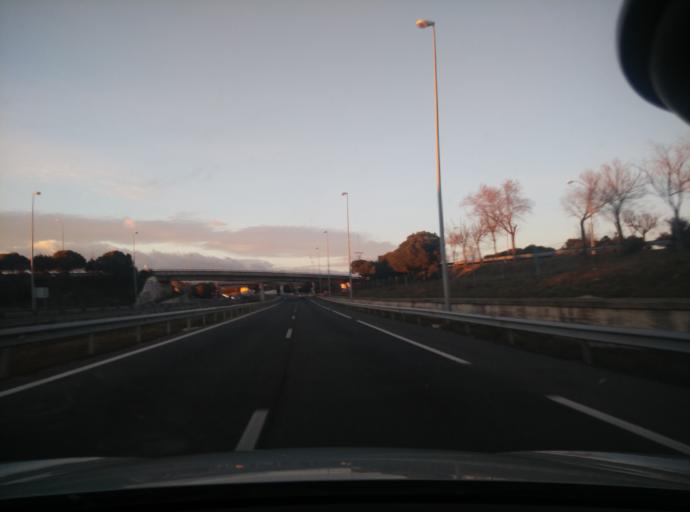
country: ES
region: Madrid
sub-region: Provincia de Madrid
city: Tres Cantos
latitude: 40.6060
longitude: -3.7205
